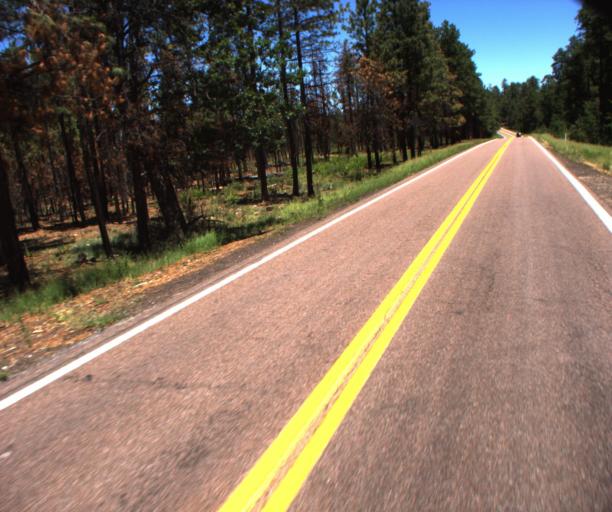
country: US
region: Arizona
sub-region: Gila County
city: Pine
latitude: 34.4426
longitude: -111.4534
